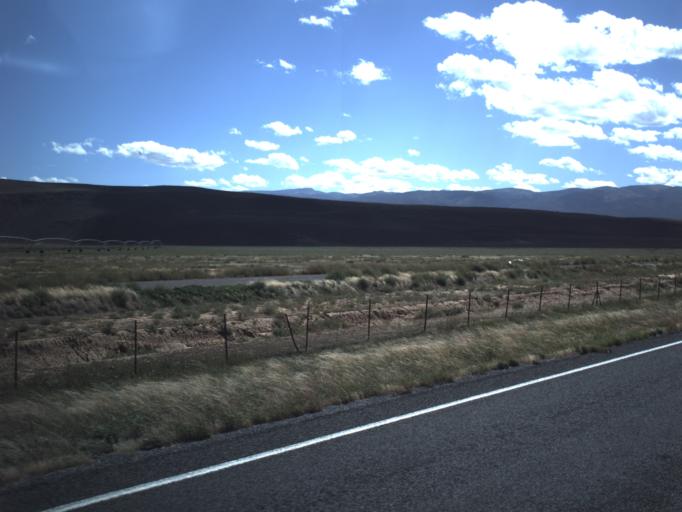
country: US
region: Utah
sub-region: Iron County
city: Enoch
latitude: 37.8823
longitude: -113.0316
